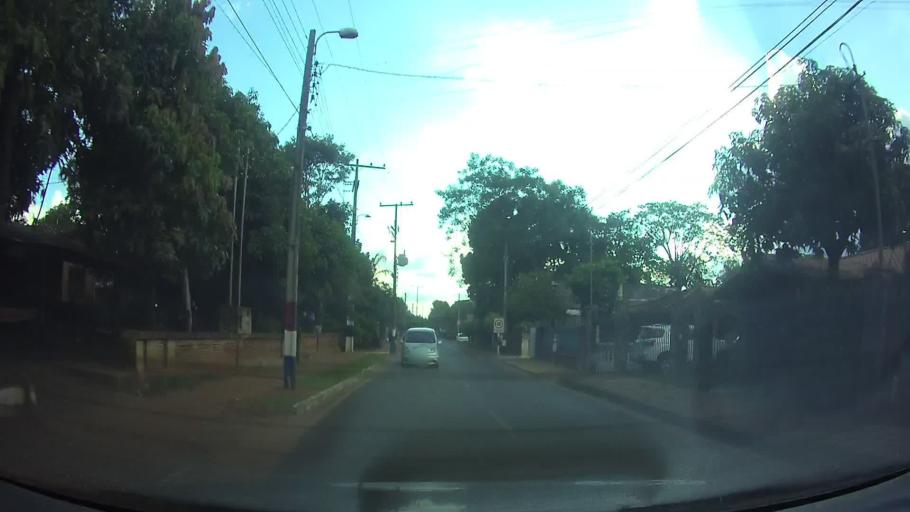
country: PY
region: Central
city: Aregua
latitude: -25.2847
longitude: -57.4375
